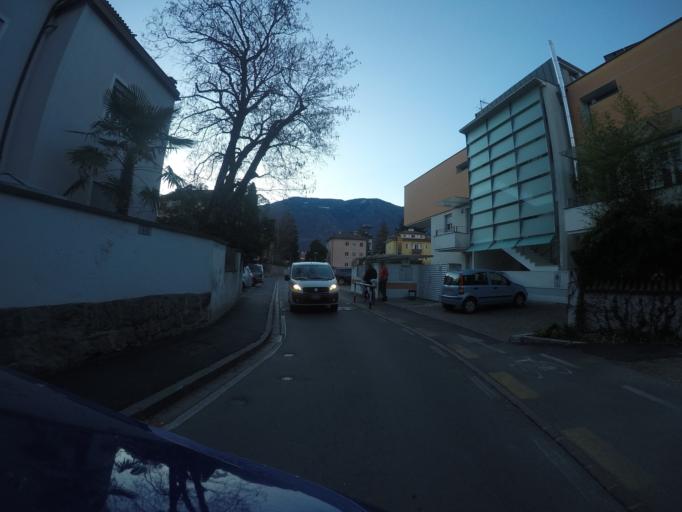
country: IT
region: Trentino-Alto Adige
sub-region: Bolzano
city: Bolzano
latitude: 46.5066
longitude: 11.3428
